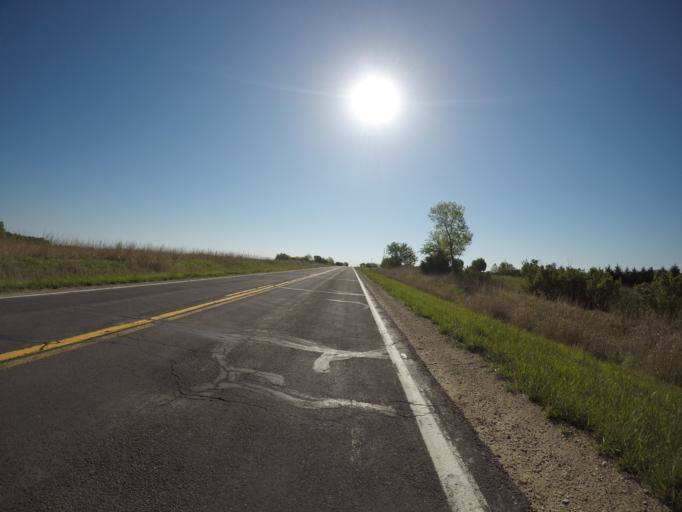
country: US
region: Kansas
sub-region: Jefferson County
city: Oskaloosa
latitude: 39.0438
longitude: -95.4440
